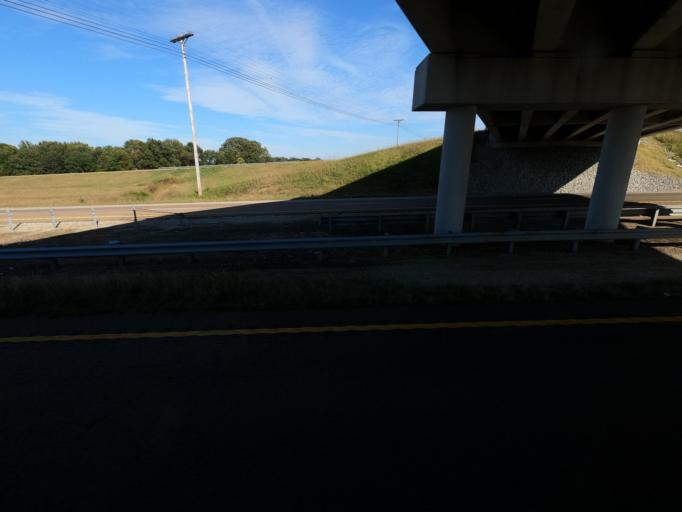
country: US
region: Tennessee
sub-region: Crockett County
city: Alamo
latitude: 35.7966
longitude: -89.1597
